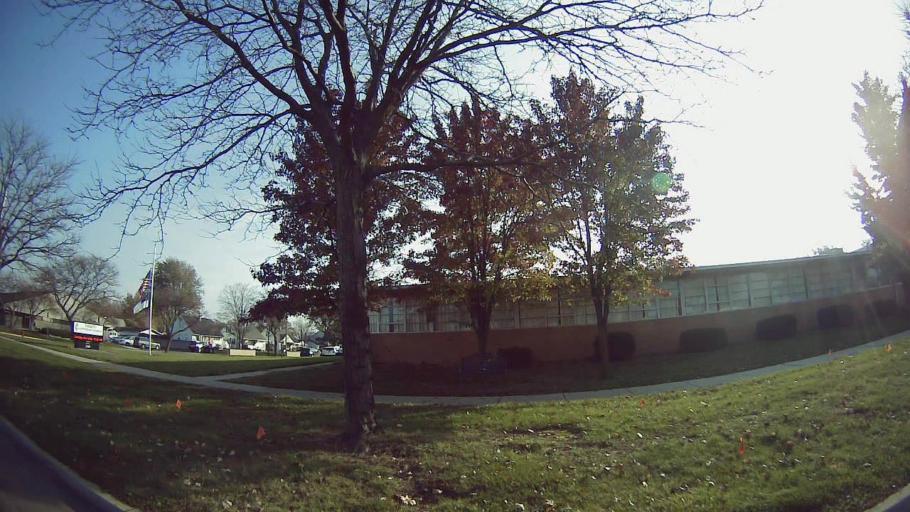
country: US
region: Michigan
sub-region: Oakland County
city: Clawson
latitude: 42.5331
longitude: -83.1577
